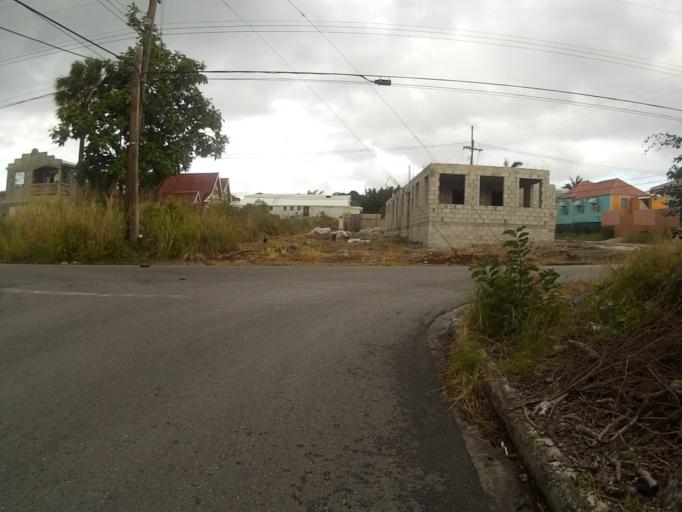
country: BB
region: Saint Michael
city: Bridgetown
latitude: 13.0963
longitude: -59.6041
